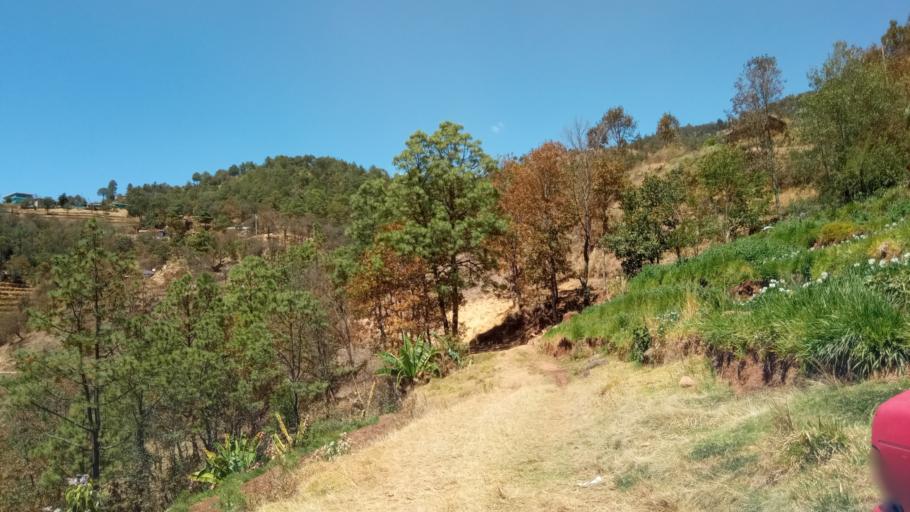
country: GT
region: San Marcos
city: Tejutla
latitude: 15.1349
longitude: -91.7899
